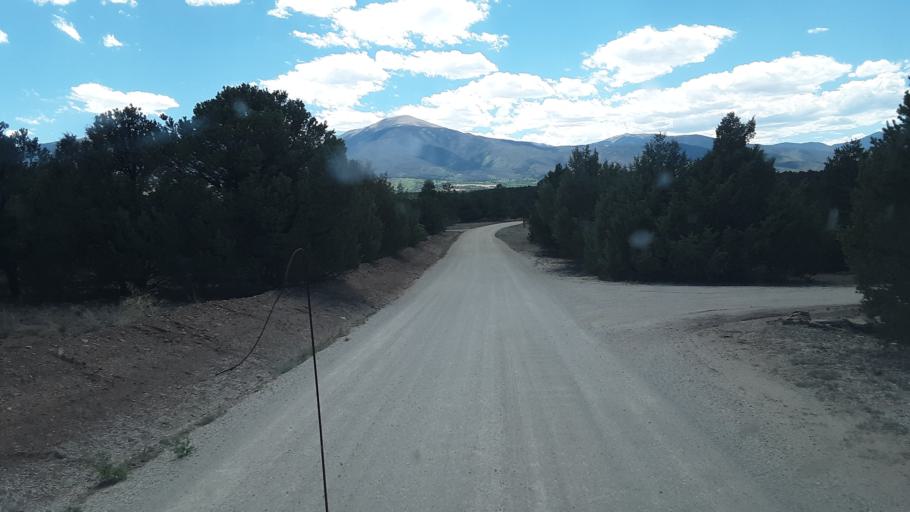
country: US
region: Colorado
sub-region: Custer County
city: Westcliffe
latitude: 38.3151
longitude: -105.6282
